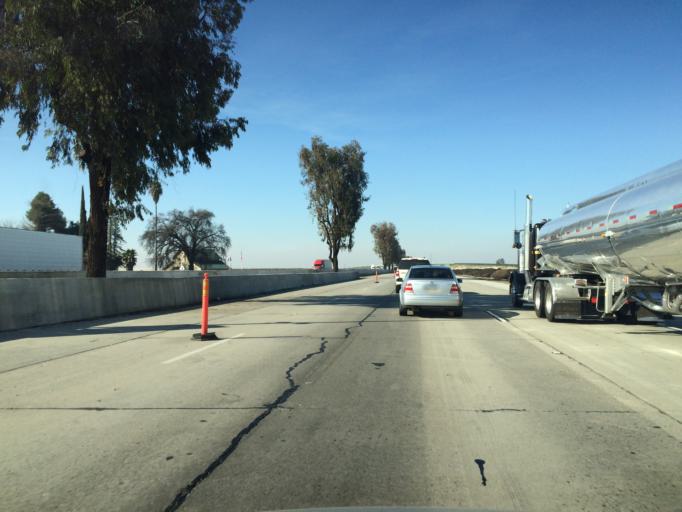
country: US
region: California
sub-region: Tulare County
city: Goshen
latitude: 36.3781
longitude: -119.4390
